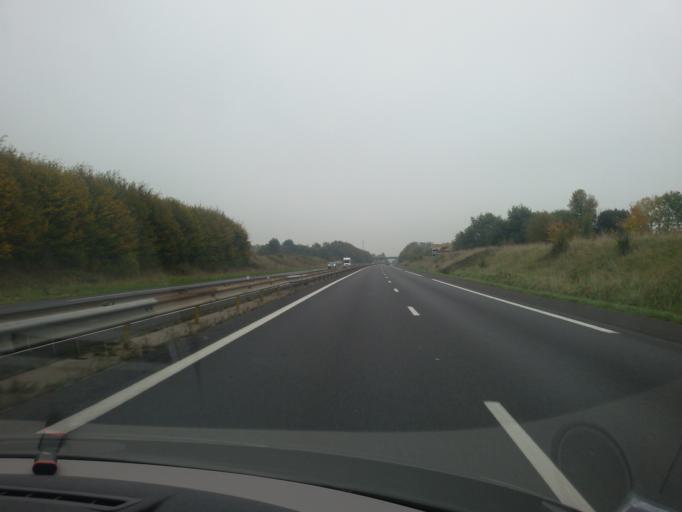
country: FR
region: Lower Normandy
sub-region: Departement du Calvados
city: Touques
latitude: 49.2622
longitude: 0.1327
